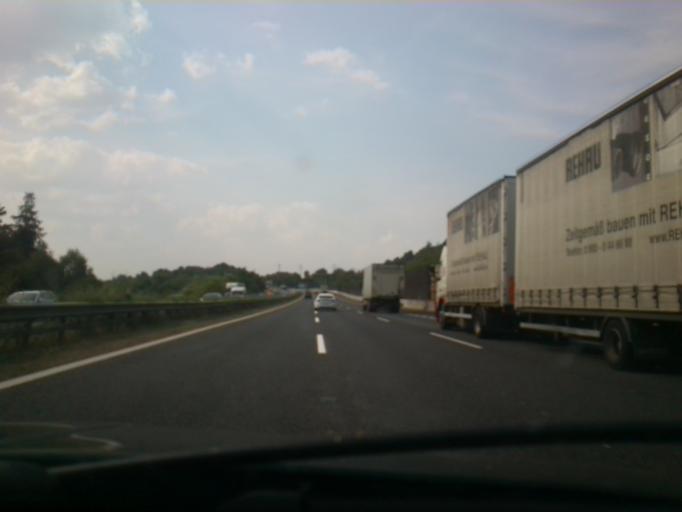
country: CZ
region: Central Bohemia
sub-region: Okres Praha-Vychod
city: Mnichovice
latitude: 49.9335
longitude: 14.6904
